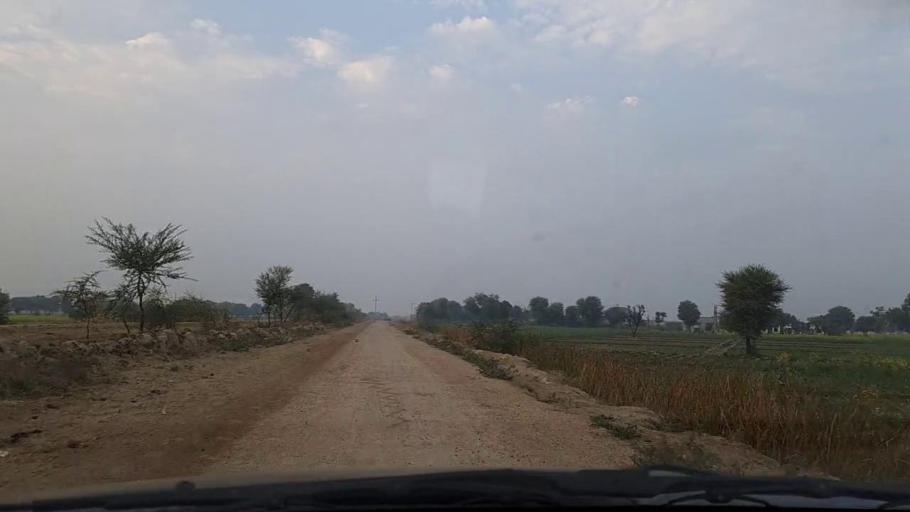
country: PK
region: Sindh
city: Pithoro
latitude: 25.5999
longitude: 69.4606
